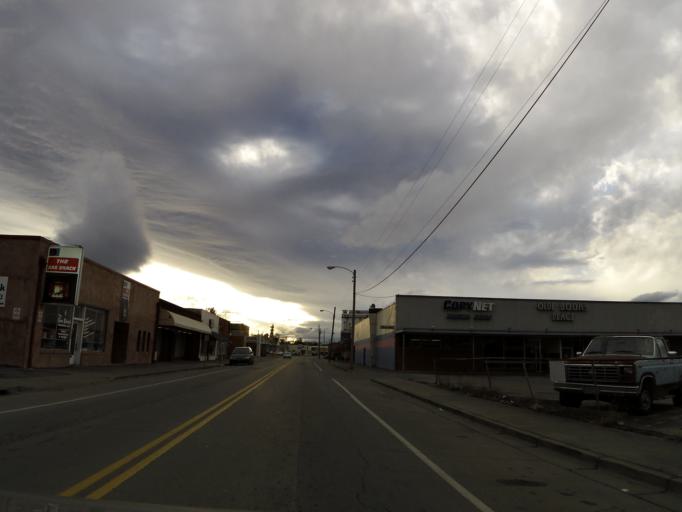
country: US
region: Tennessee
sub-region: Washington County
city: Johnson City
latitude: 36.3124
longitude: -82.3534
